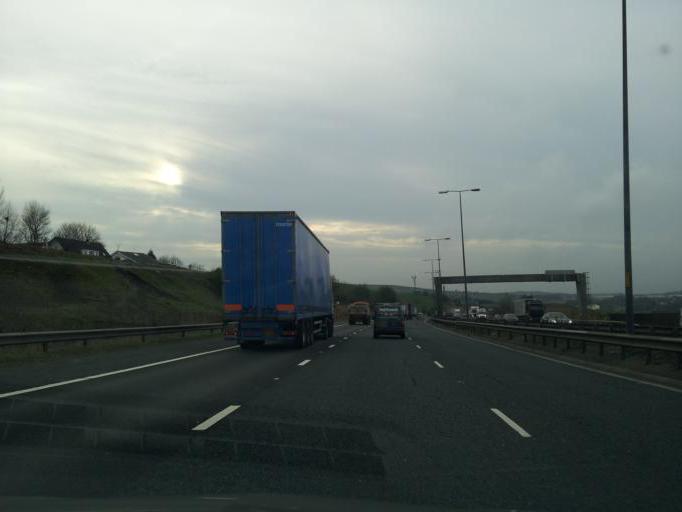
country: GB
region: England
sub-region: Borough of Rochdale
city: Milnrow
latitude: 53.6098
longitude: -2.0927
